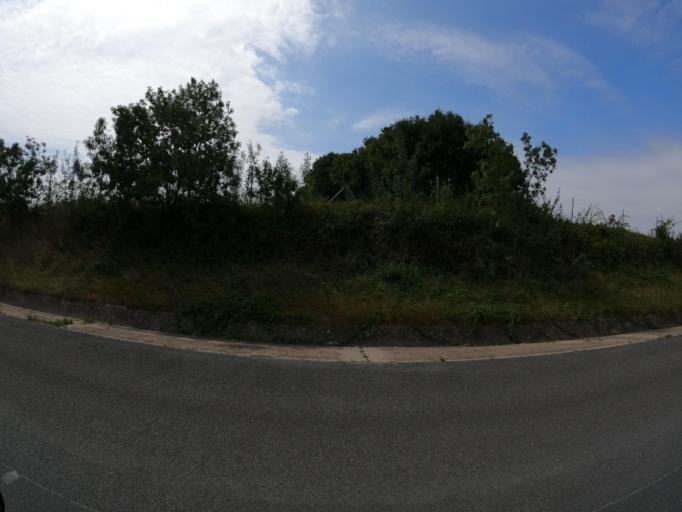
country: FR
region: Poitou-Charentes
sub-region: Departement de la Charente-Maritime
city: Saint-Jean-de-Liversay
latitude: 46.2252
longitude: -0.8657
